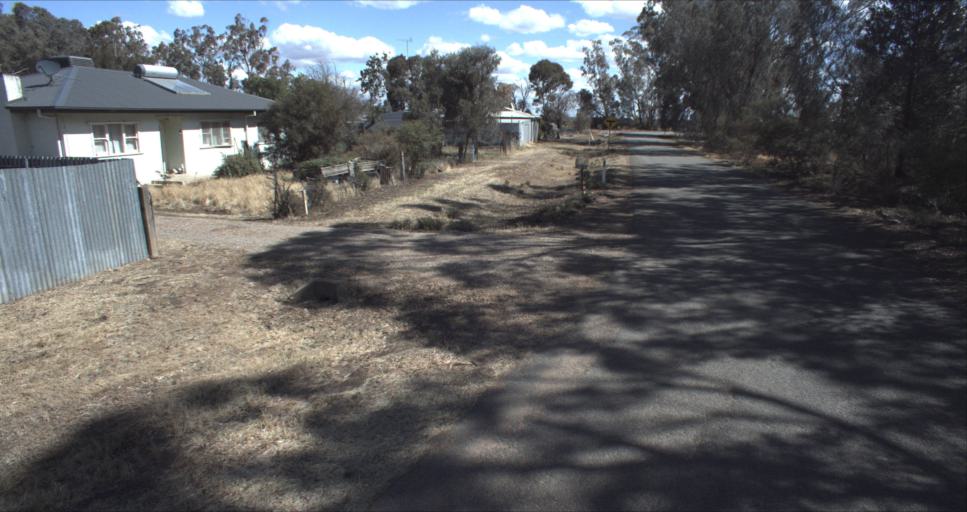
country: AU
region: New South Wales
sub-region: Leeton
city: Leeton
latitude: -34.5164
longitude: 146.2336
